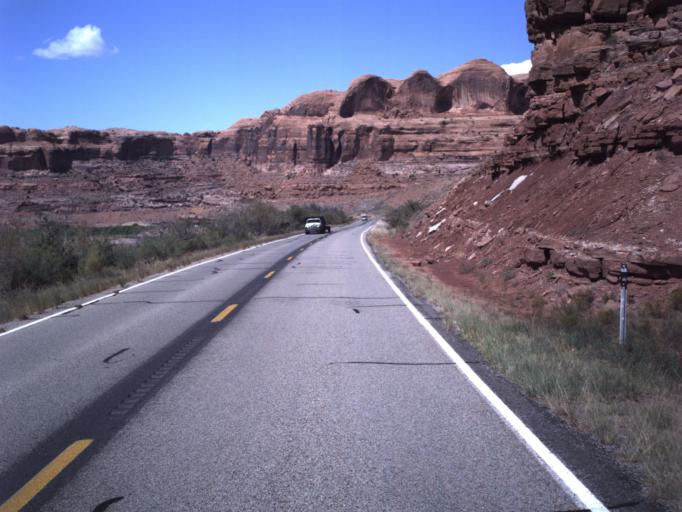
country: US
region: Utah
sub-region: Grand County
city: Moab
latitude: 38.5697
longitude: -109.6323
